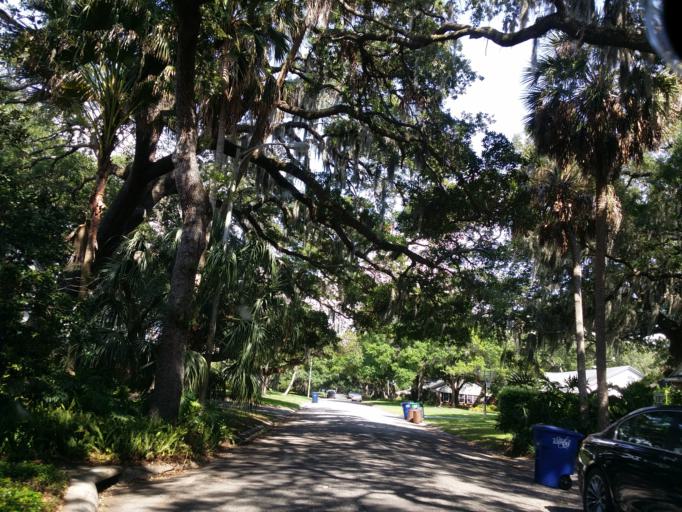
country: US
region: Florida
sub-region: Hillsborough County
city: Tampa
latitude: 27.9328
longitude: -82.5225
